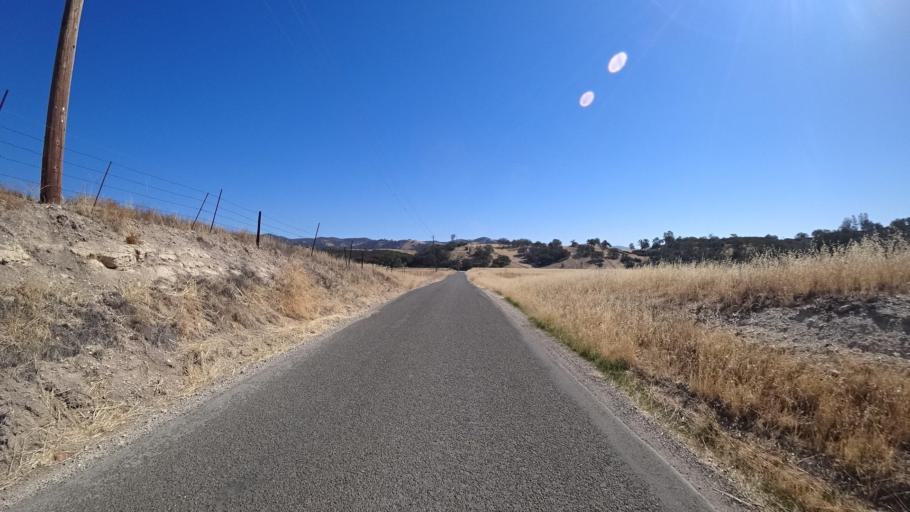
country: US
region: California
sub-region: Monterey County
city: King City
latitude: 36.0109
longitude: -121.1613
